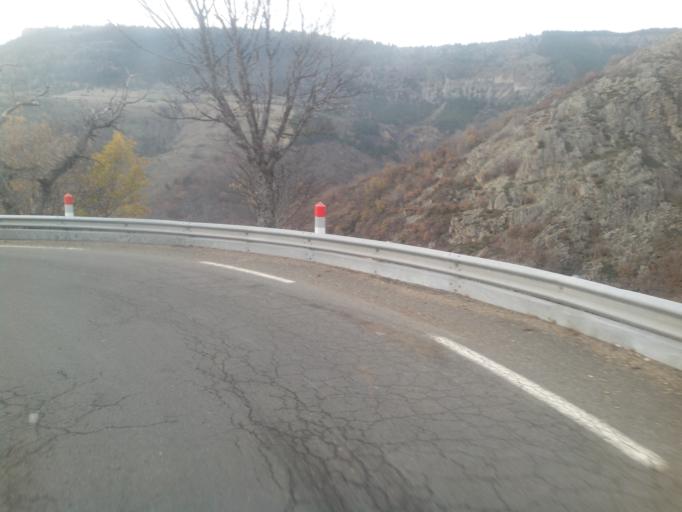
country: FR
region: Languedoc-Roussillon
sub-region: Departement de la Lozere
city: Florac
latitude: 44.3973
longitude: 3.5627
